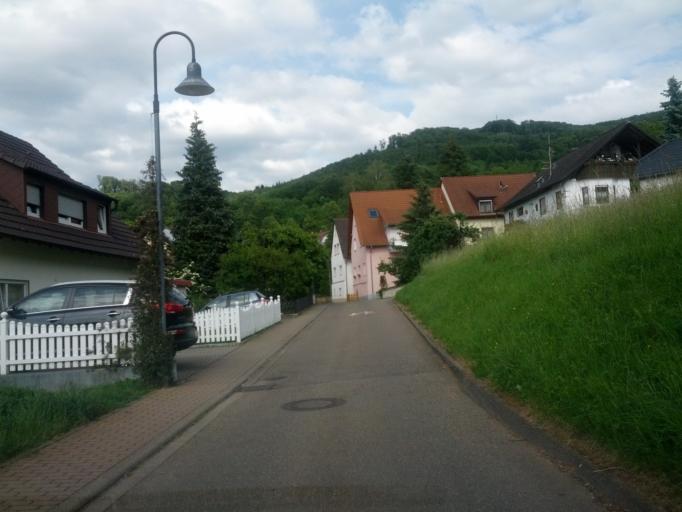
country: DE
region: Baden-Wuerttemberg
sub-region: Freiburg Region
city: Ebringen
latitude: 47.9559
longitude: 7.7868
